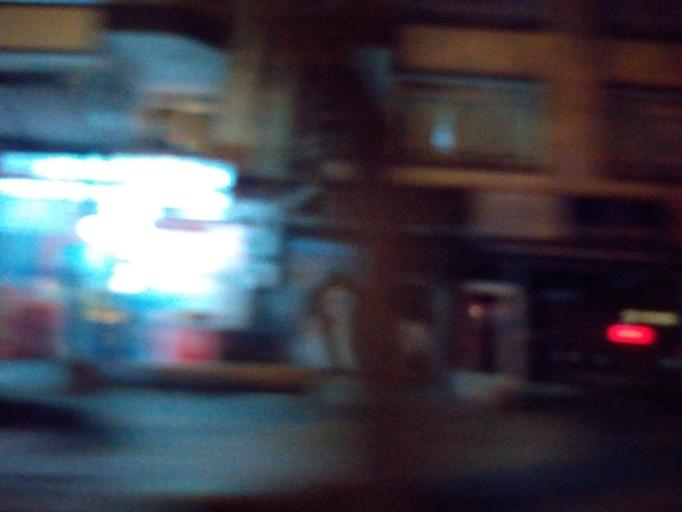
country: TR
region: Ankara
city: Ankara
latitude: 39.9800
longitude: 32.8292
